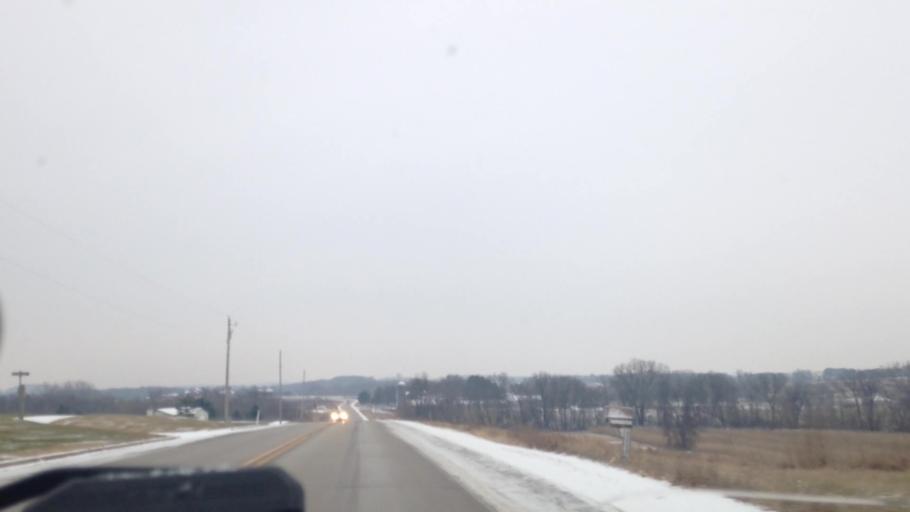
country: US
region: Wisconsin
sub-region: Dodge County
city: Hustisford
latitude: 43.3826
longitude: -88.5419
